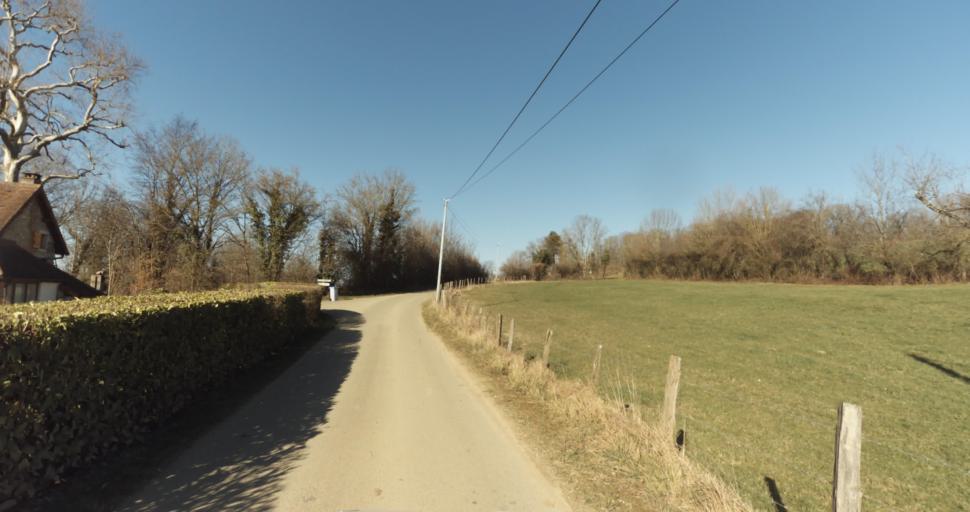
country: FR
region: Franche-Comte
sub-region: Departement du Jura
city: Montmorot
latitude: 46.6984
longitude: 5.5177
